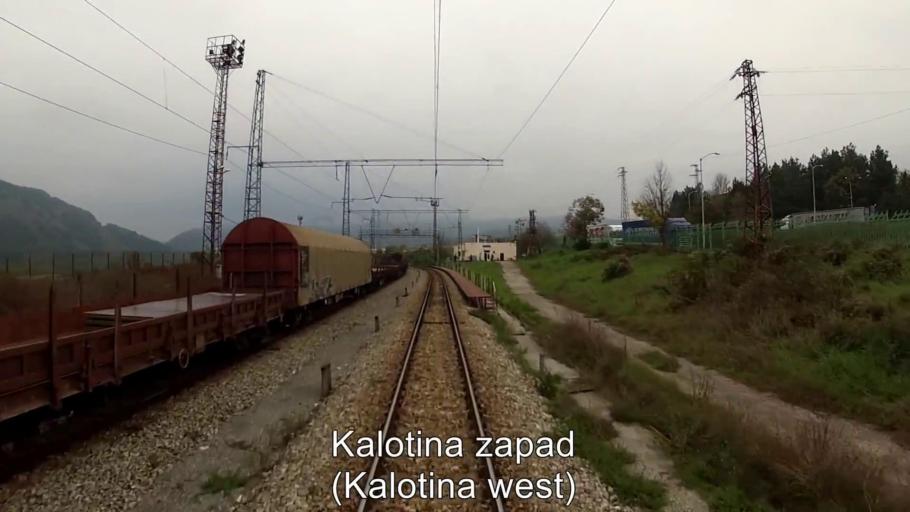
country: RS
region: Central Serbia
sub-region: Pirotski Okrug
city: Dimitrovgrad
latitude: 42.9968
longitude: 22.8383
